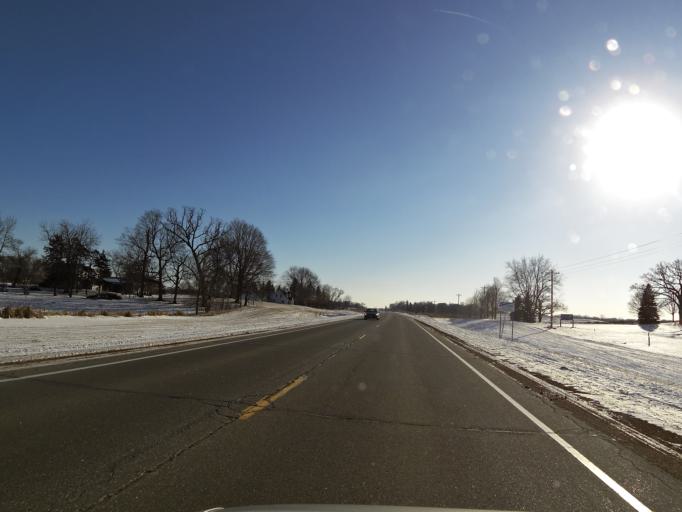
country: US
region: Minnesota
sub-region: Scott County
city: Prior Lake
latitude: 44.6374
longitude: -93.5017
